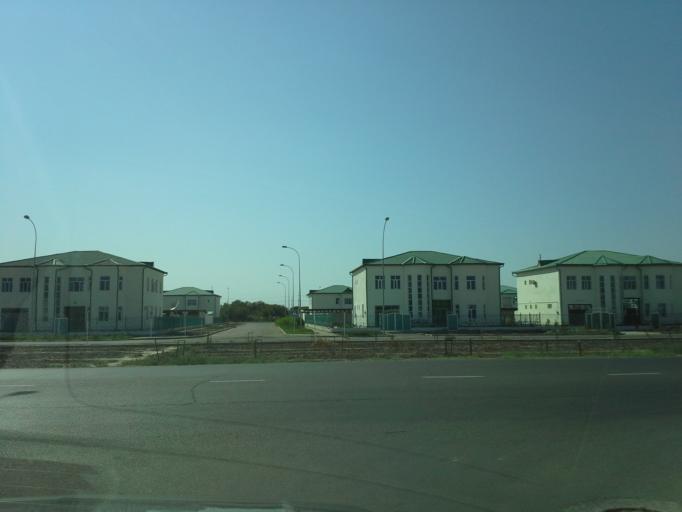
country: TM
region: Dasoguz
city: Dasoguz
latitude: 41.8178
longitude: 59.9522
